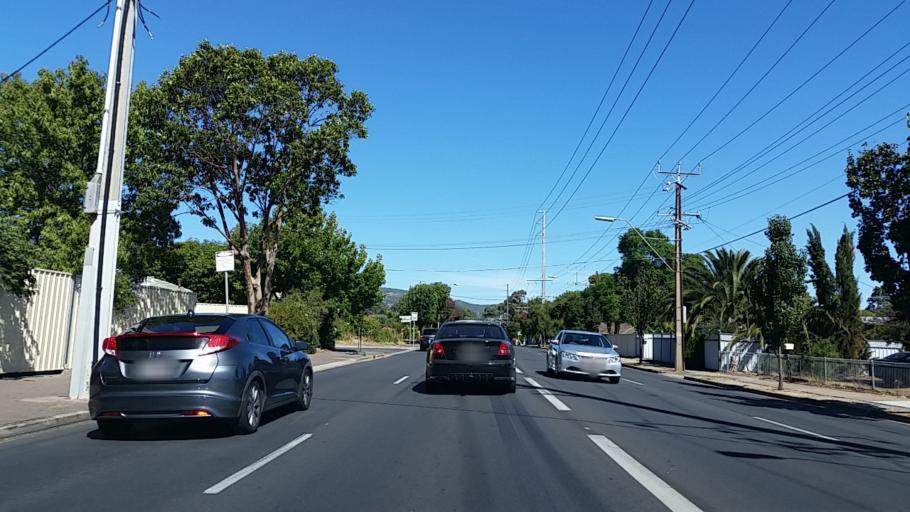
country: AU
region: South Australia
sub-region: Campbelltown
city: Campbelltown
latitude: -34.8826
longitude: 138.6738
